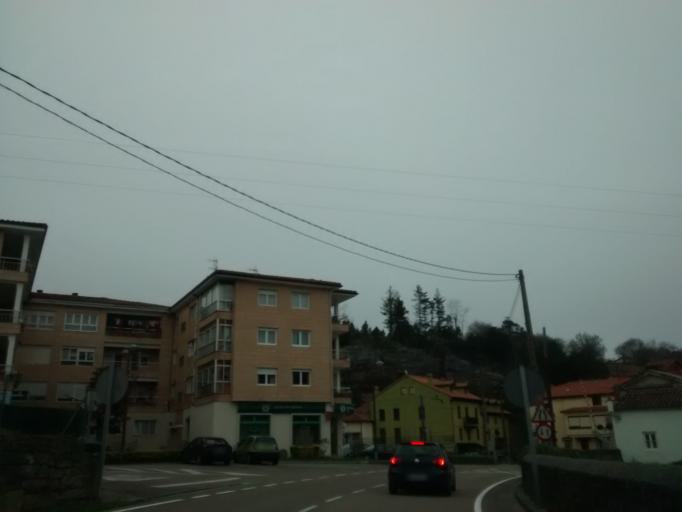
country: ES
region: Cantabria
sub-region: Provincia de Cantabria
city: Entrambasaguas
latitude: 43.3520
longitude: -3.7081
